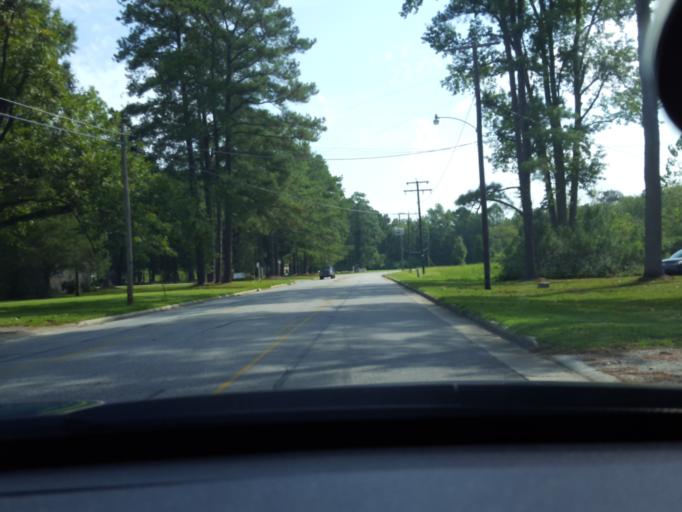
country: US
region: North Carolina
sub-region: Washington County
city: Plymouth
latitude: 35.8703
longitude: -76.7346
